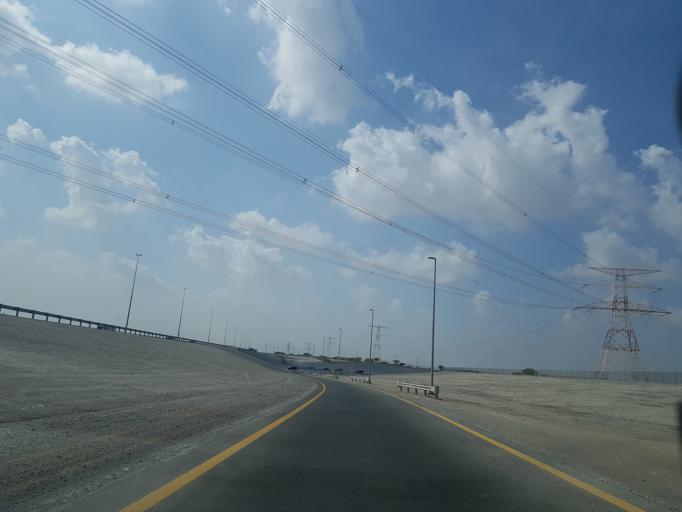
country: AE
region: Ra's al Khaymah
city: Ras al-Khaimah
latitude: 25.7659
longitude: 56.0234
